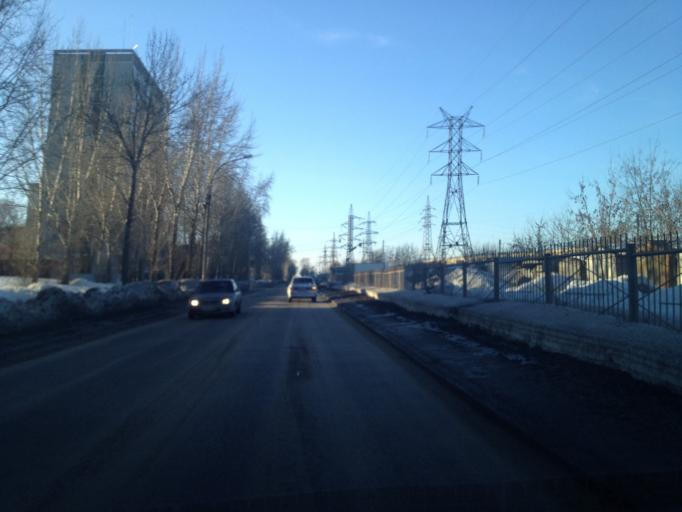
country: RU
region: Sverdlovsk
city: Yekaterinburg
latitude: 56.8700
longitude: 60.5633
